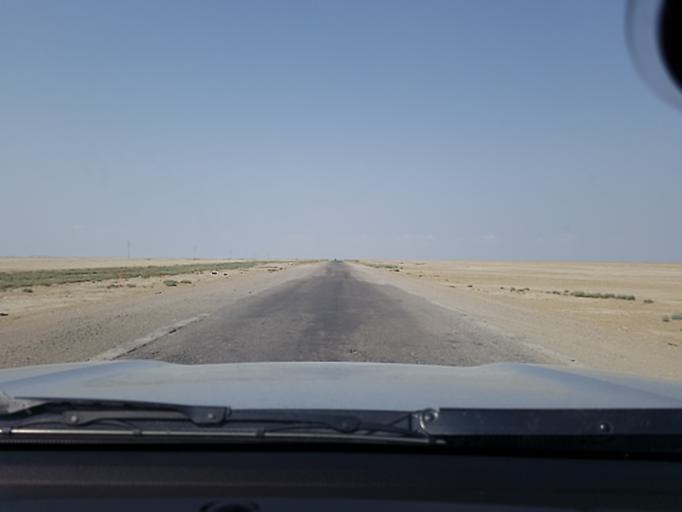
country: TM
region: Balkan
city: Gumdag
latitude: 38.7226
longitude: 54.4793
